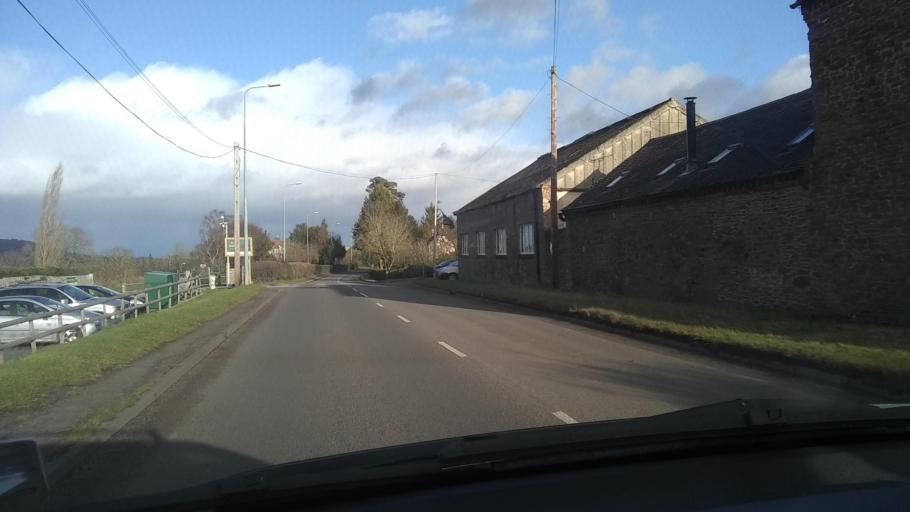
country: GB
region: England
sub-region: Worcestershire
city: Bewdley
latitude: 52.3700
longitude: -2.3384
